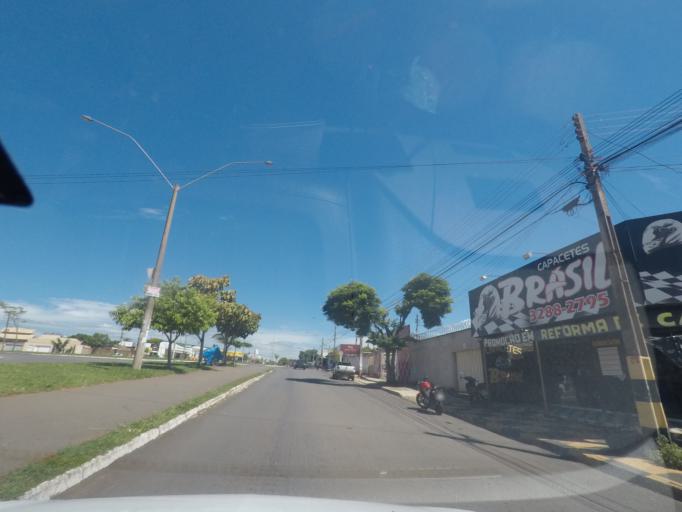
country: BR
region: Goias
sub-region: Aparecida De Goiania
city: Aparecida de Goiania
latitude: -16.7703
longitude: -49.3428
